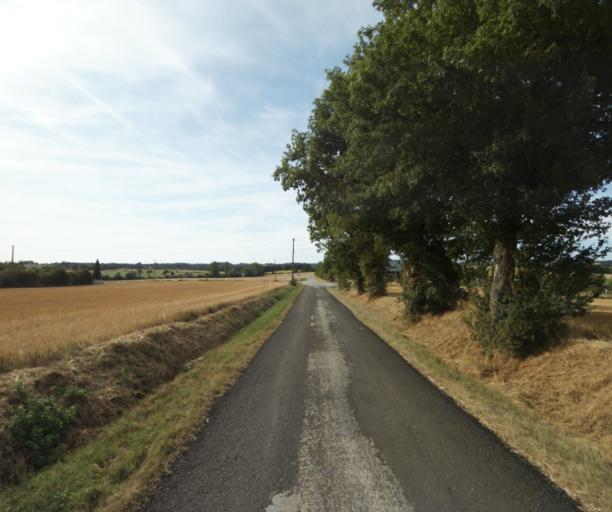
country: FR
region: Midi-Pyrenees
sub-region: Departement du Tarn
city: Puylaurens
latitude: 43.5240
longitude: 2.0410
